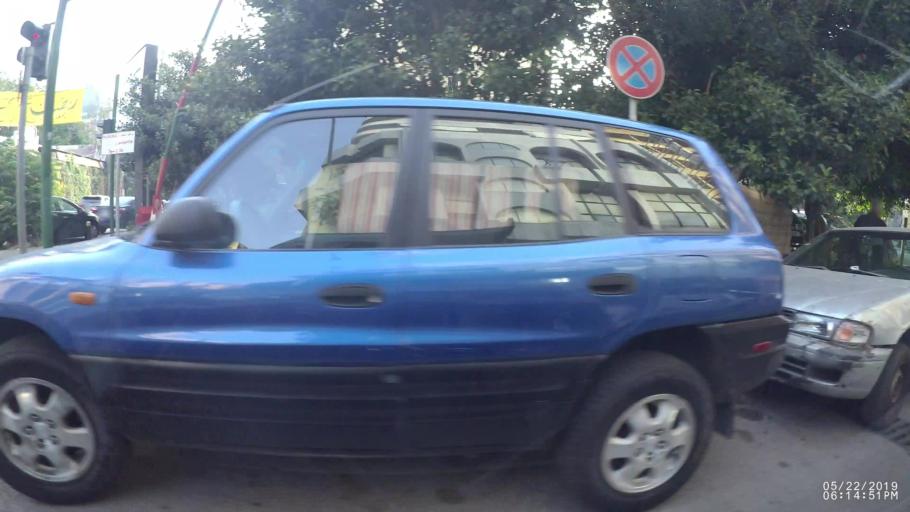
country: LB
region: Beyrouth
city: Ra's Bayrut
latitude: 33.8964
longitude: 35.4773
